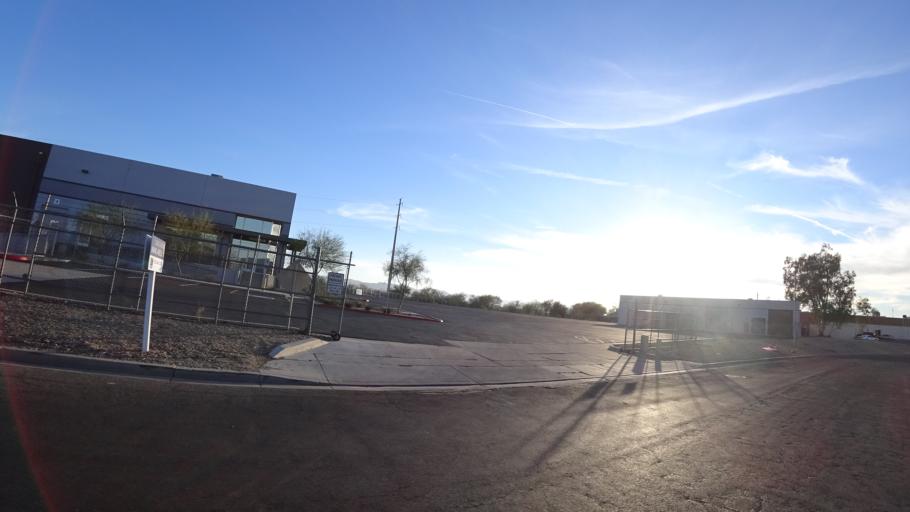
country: US
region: Arizona
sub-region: Maricopa County
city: Phoenix
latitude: 33.4233
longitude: -112.0682
